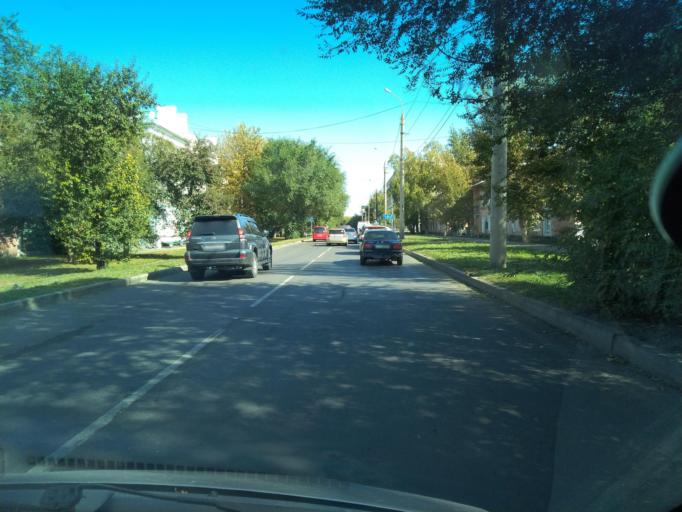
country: RU
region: Krasnoyarskiy
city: Krasnoyarsk
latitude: 56.0050
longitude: 92.9618
